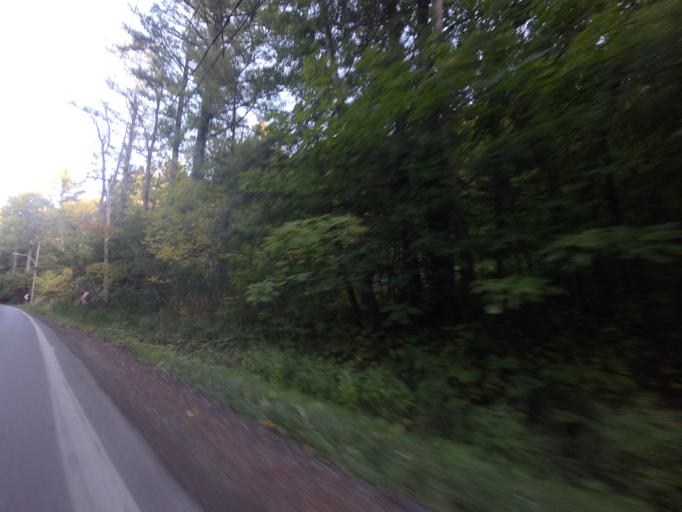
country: CA
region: Quebec
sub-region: Monteregie
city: Hudson
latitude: 45.4685
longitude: -74.1690
